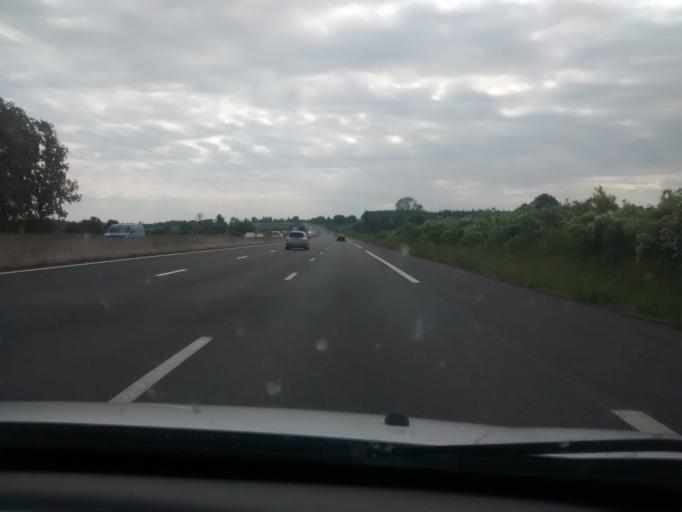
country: FR
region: Pays de la Loire
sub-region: Departement de la Sarthe
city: Cherre
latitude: 48.1418
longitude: 0.6607
